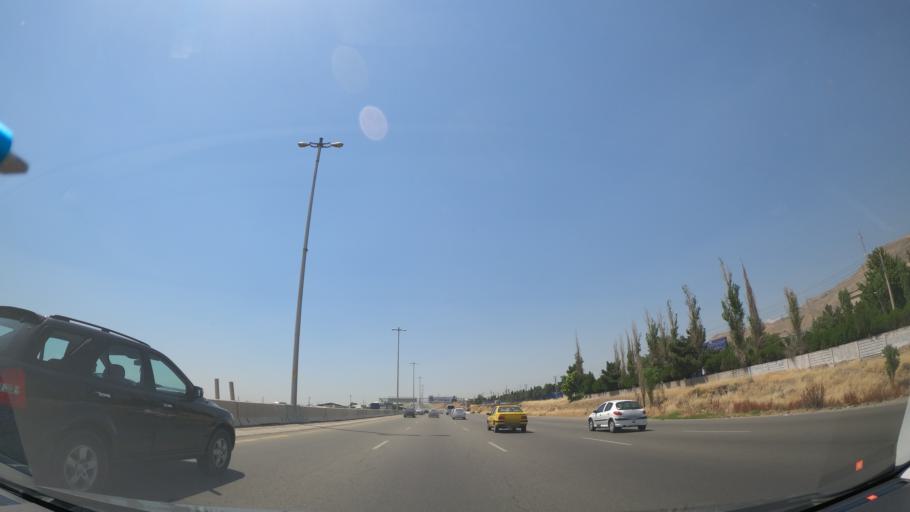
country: IR
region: Tehran
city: Shahr-e Qods
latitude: 35.7624
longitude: 51.0613
